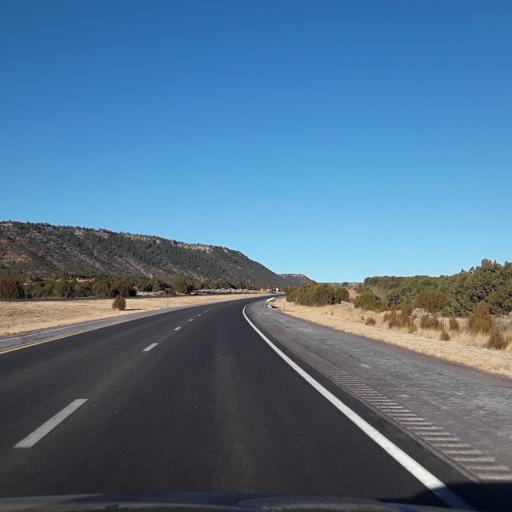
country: US
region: New Mexico
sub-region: San Miguel County
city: Pecos
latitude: 35.4292
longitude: -105.5949
